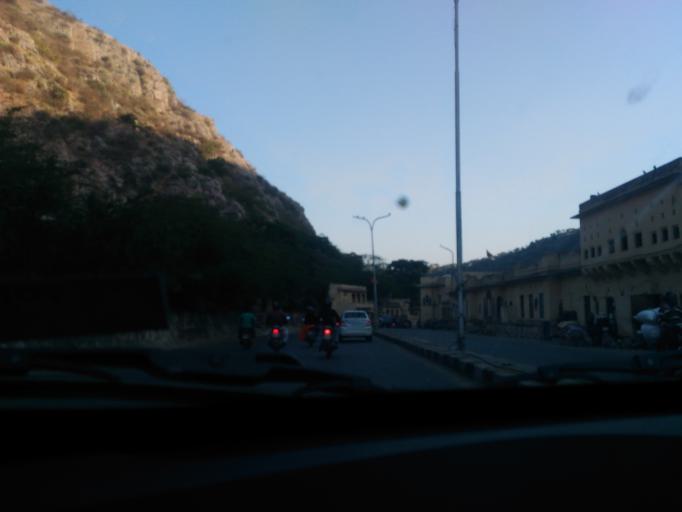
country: IN
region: Rajasthan
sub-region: Jaipur
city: Jaipur
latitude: 26.9012
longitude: 75.8527
